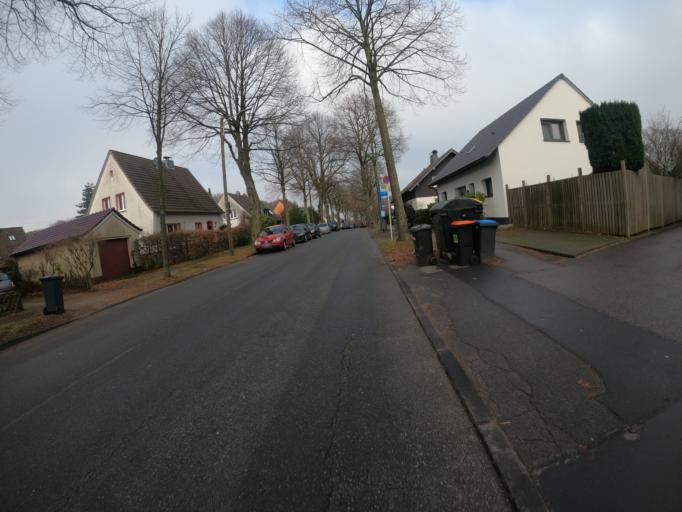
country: DE
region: North Rhine-Westphalia
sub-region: Regierungsbezirk Dusseldorf
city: Wuppertal
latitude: 51.2302
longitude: 7.1343
